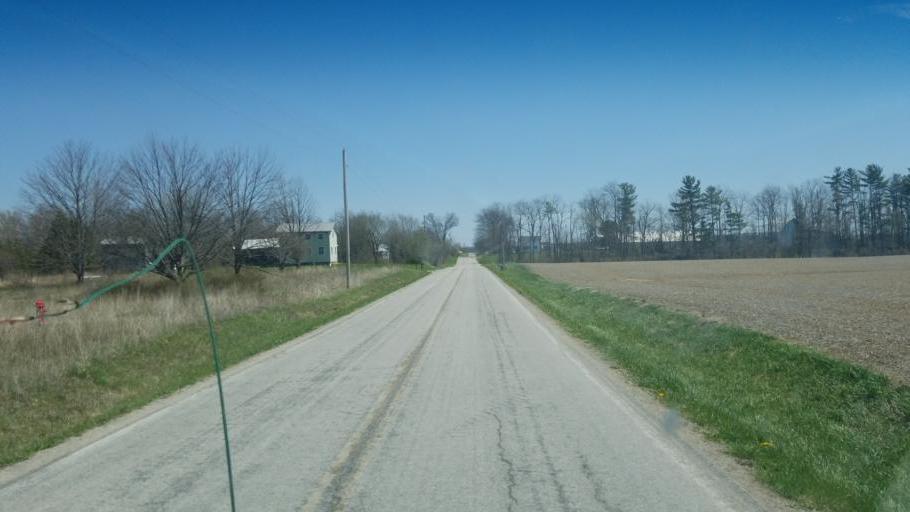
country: US
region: Ohio
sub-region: Huron County
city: New London
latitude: 41.1019
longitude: -82.3603
